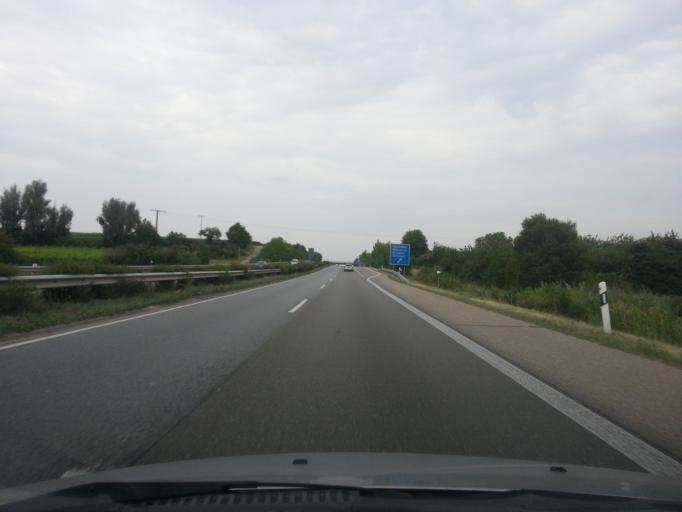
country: DE
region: Rheinland-Pfalz
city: Kirrweiler
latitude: 49.2917
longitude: 8.1522
